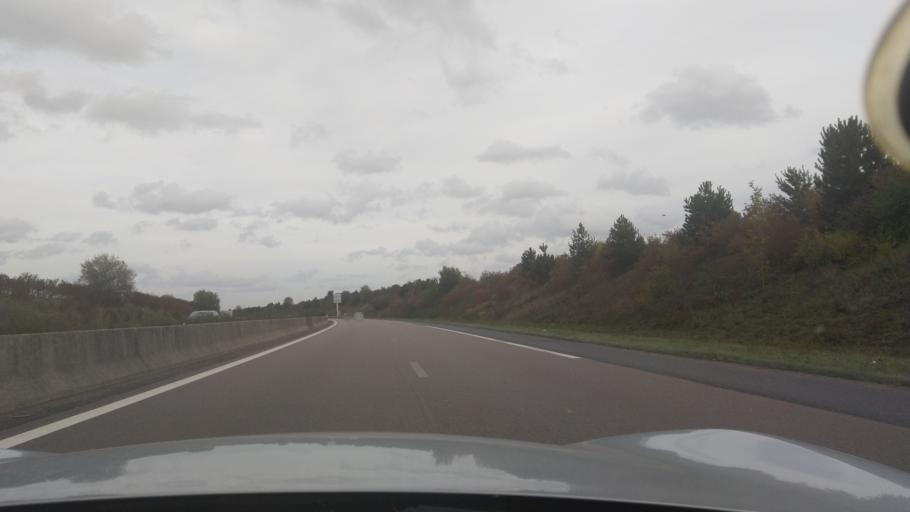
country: FR
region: Ile-de-France
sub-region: Departement du Val-d'Oise
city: Louvres
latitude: 49.0272
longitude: 2.5086
